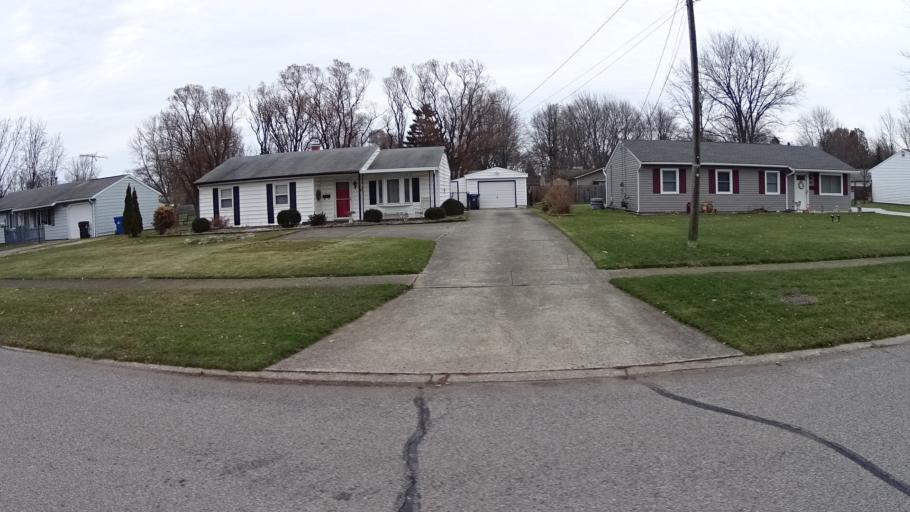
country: US
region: Ohio
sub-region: Lorain County
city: North Ridgeville
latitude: 41.3841
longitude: -82.0091
